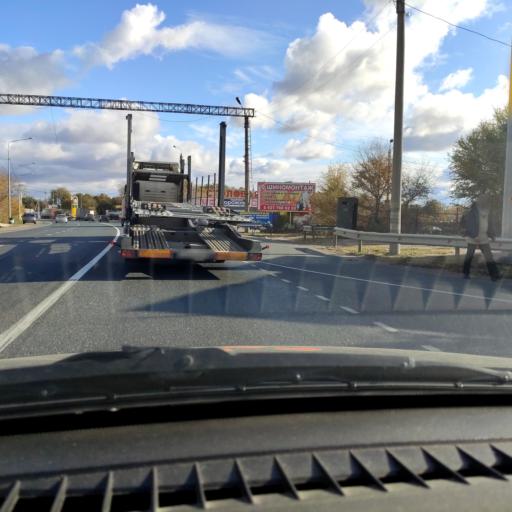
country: RU
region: Samara
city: Varlamovo
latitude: 53.1909
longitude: 48.3551
